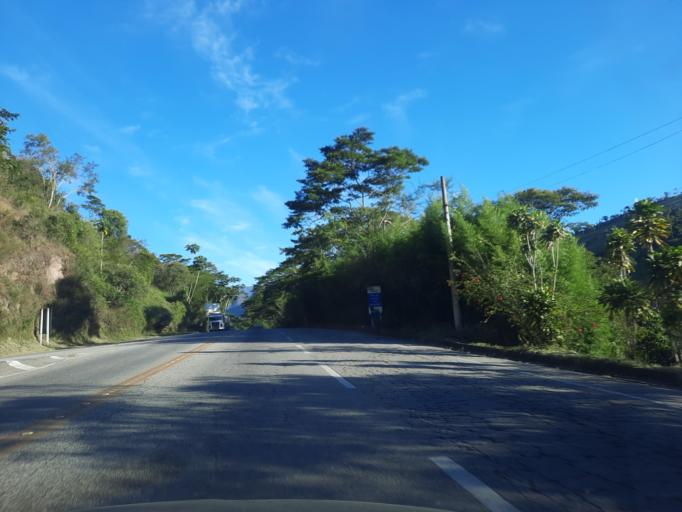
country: BR
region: Rio de Janeiro
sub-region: Petropolis
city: Petropolis
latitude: -22.4095
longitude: -43.1453
